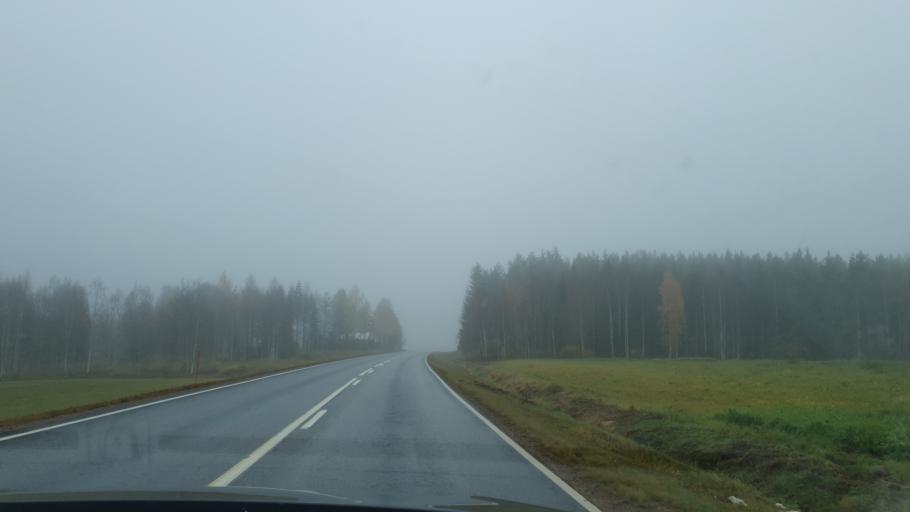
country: FI
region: Lapland
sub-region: Rovaniemi
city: Rovaniemi
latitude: 66.8054
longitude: 25.4125
